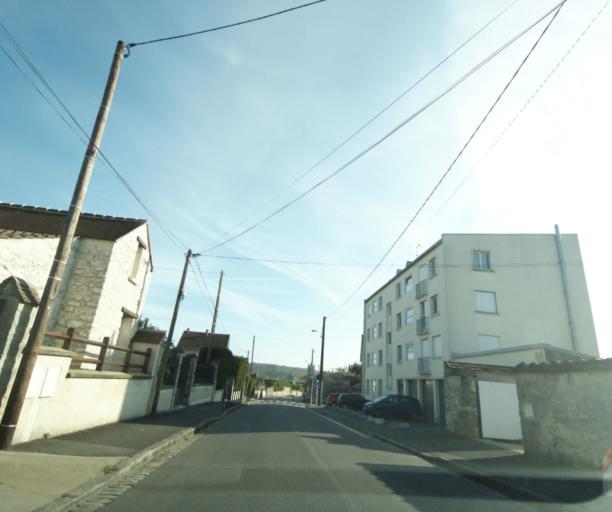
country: FR
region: Ile-de-France
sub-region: Departement de Seine-et-Marne
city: Moret-sur-Loing
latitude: 48.3692
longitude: 2.8143
